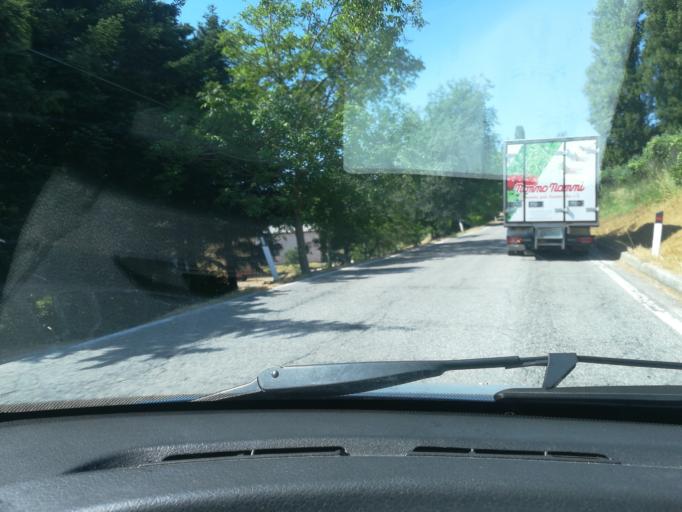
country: IT
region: The Marches
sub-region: Provincia di Macerata
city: San Ginesio
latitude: 43.1081
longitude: 13.3377
